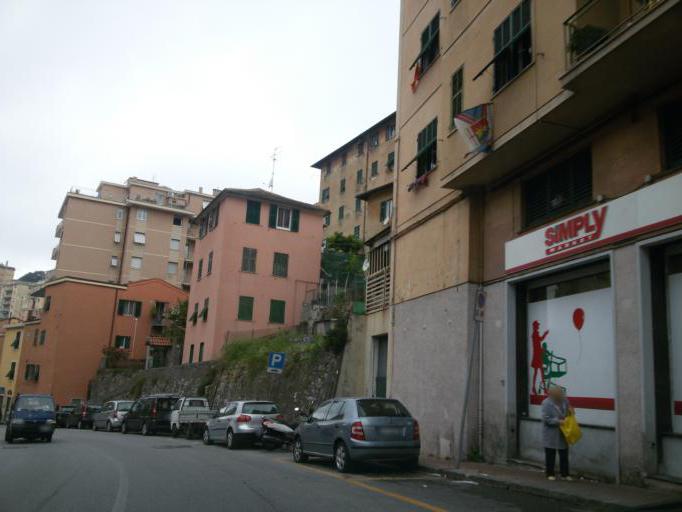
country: IT
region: Liguria
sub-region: Provincia di Genova
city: Genoa
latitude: 44.4205
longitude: 8.9698
